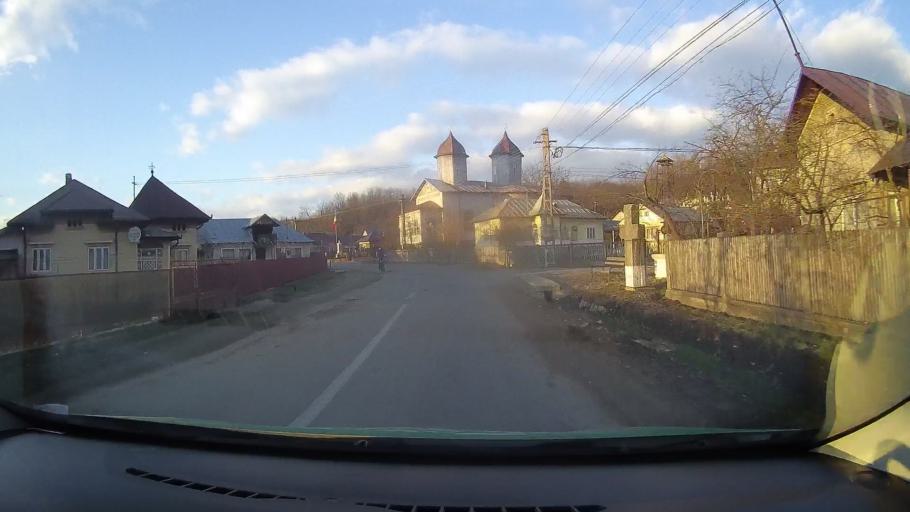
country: RO
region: Dambovita
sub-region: Comuna Gura Ocnitei
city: Adanca
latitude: 44.9184
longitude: 25.6163
